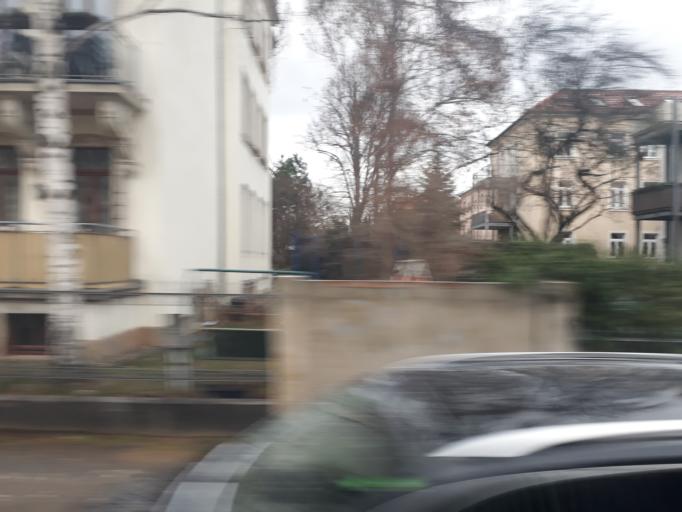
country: DE
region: Saxony
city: Albertstadt
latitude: 51.0491
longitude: 13.7990
